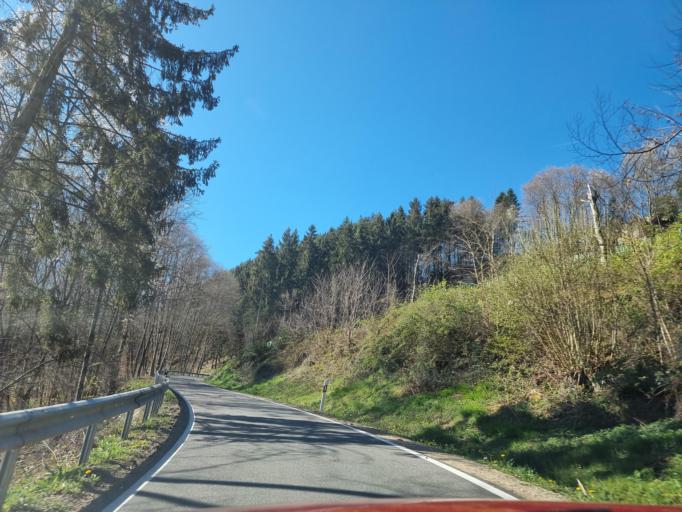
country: DE
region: Rheinland-Pfalz
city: Prumzurlay
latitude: 49.8670
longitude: 6.4304
